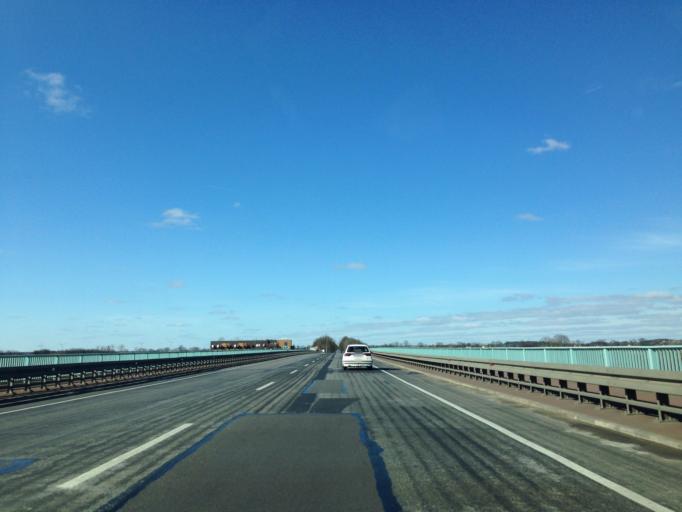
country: PL
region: Pomeranian Voivodeship
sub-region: Powiat malborski
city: Lisewo Malborskie
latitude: 54.0522
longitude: 18.8189
